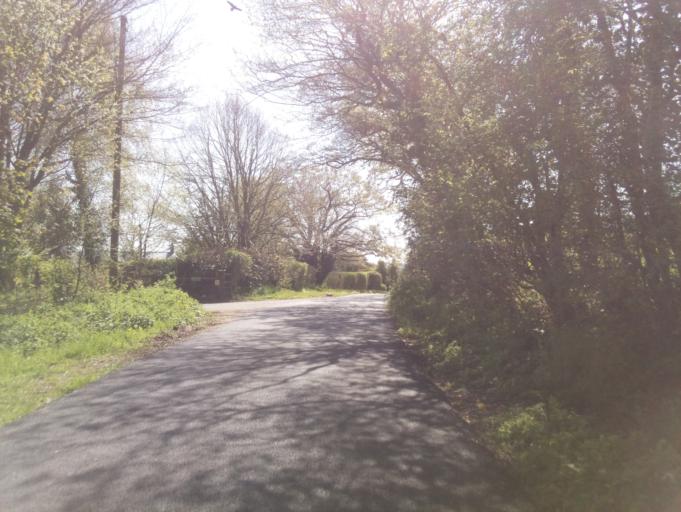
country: GB
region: Wales
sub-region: Monmouthshire
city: Llangwm
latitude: 51.7473
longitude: -2.8304
